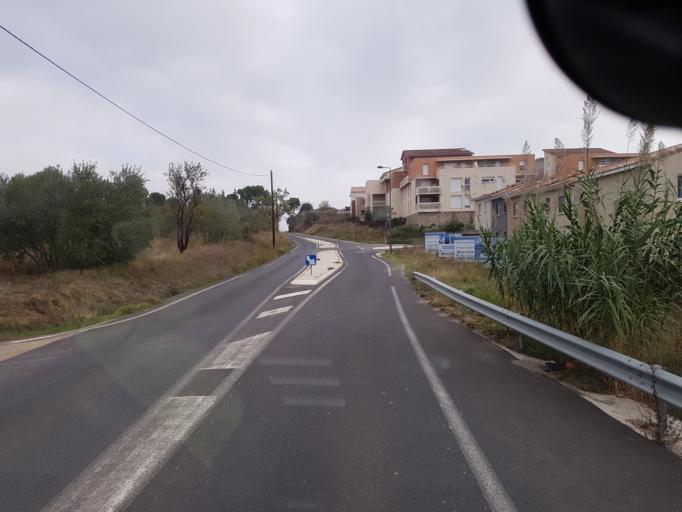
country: FR
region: Languedoc-Roussillon
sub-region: Departement de l'Herault
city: Meze
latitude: 43.4426
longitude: 3.5800
